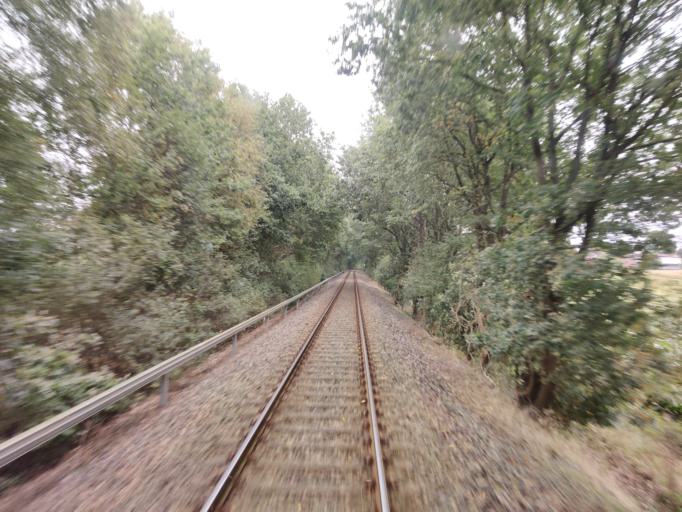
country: DE
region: Lower Saxony
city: Kutenholz
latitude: 53.4868
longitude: 9.2631
